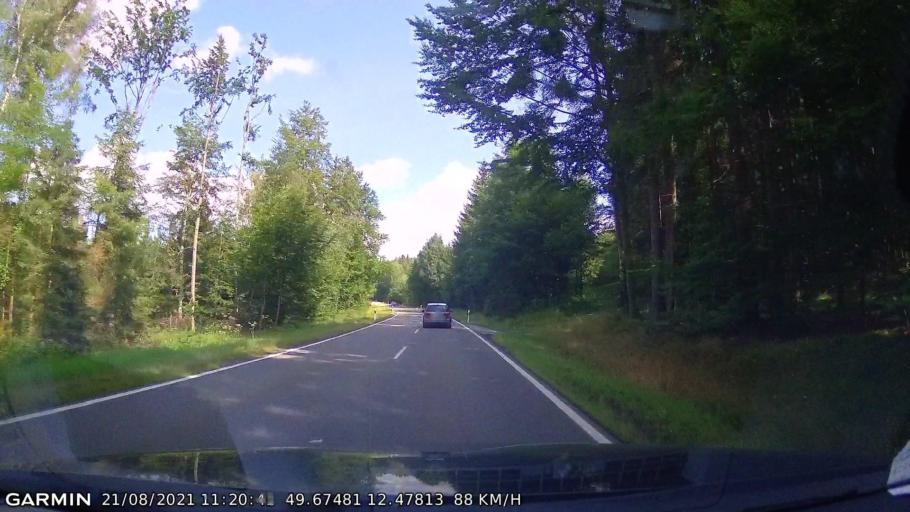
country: DE
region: Bavaria
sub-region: Upper Palatinate
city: Waidhaus
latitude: 49.6749
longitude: 12.4782
